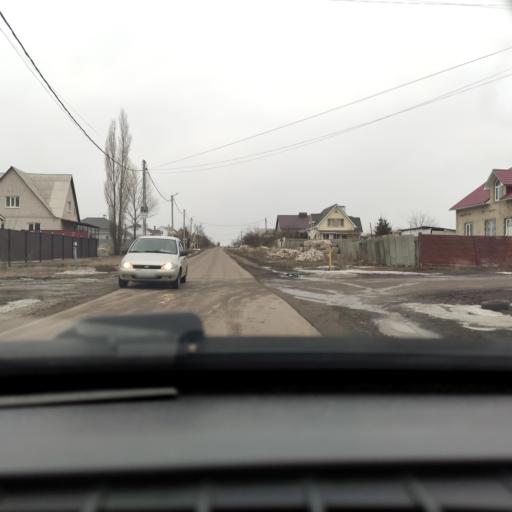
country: RU
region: Voronezj
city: Novaya Usman'
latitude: 51.6566
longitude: 39.4101
